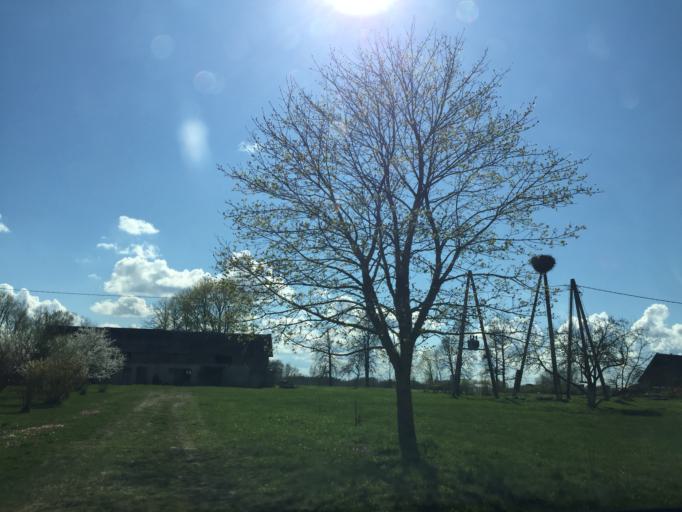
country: LV
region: Strenci
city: Strenci
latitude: 57.5048
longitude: 25.6819
